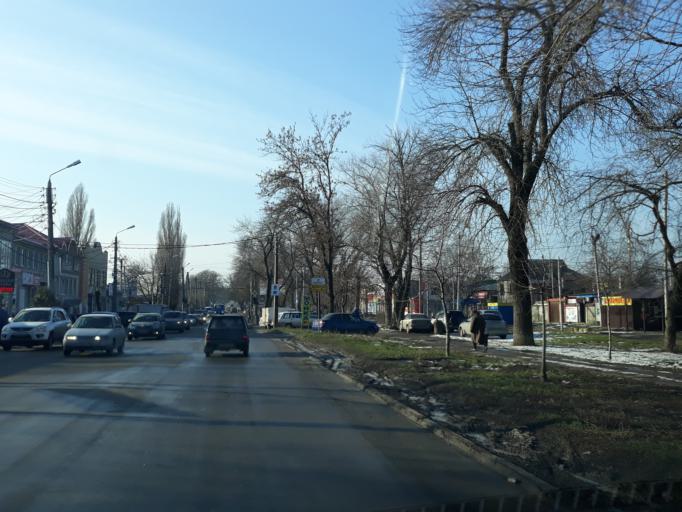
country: RU
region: Rostov
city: Taganrog
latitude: 47.2151
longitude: 38.9124
